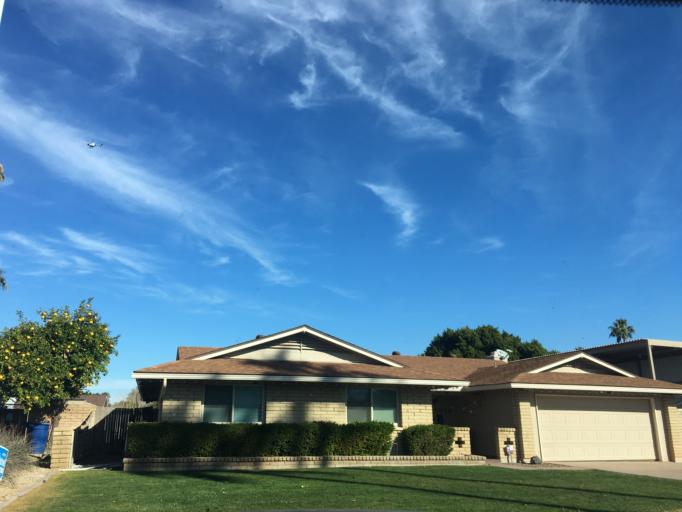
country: US
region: Arizona
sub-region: Maricopa County
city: Tempe
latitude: 33.3874
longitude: -111.9042
